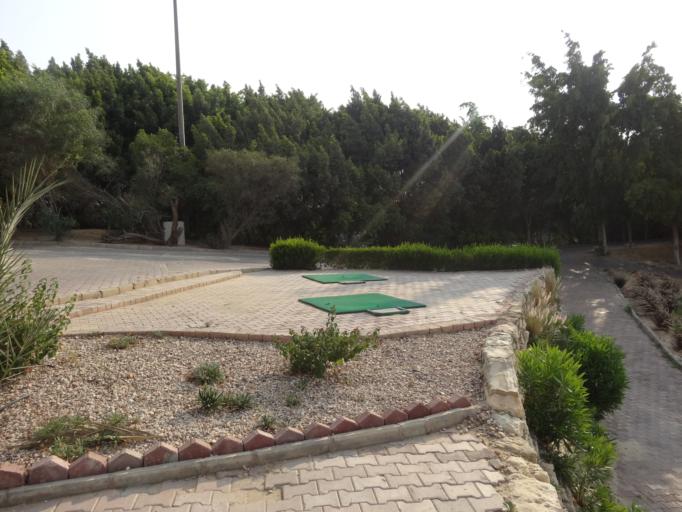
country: EG
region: Muhafazat al Qalyubiyah
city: Al Khankah
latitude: 30.0699
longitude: 31.4337
